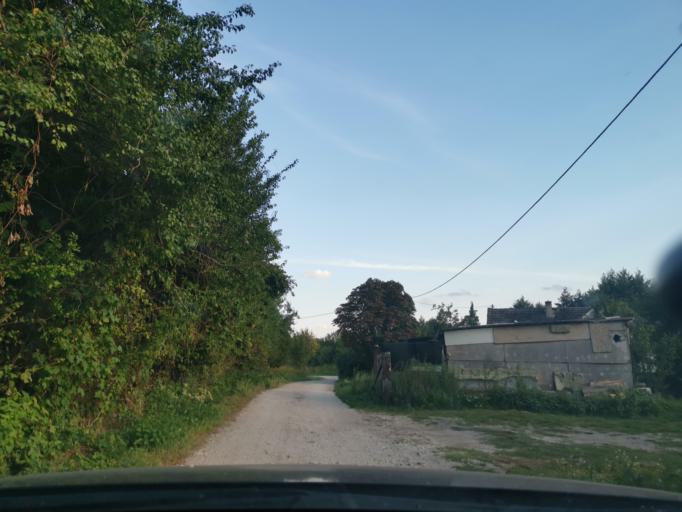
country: SK
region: Trnavsky
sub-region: Okres Senica
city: Senica
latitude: 48.6548
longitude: 17.2619
